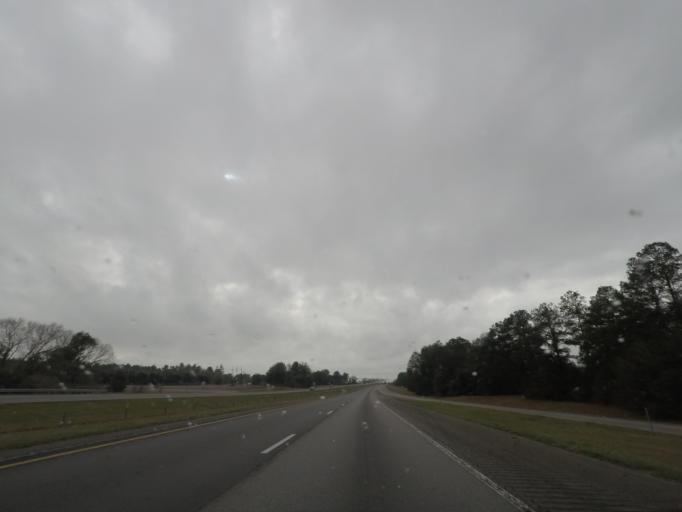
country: US
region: South Carolina
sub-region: Orangeburg County
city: Holly Hill
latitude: 33.5228
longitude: -80.4303
